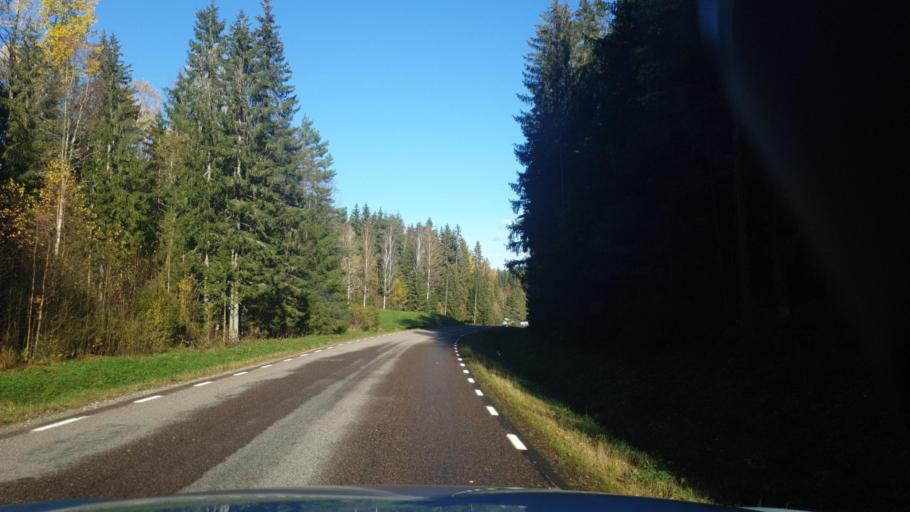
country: SE
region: Vaermland
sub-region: Arvika Kommun
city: Arvika
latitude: 59.6141
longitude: 12.7830
